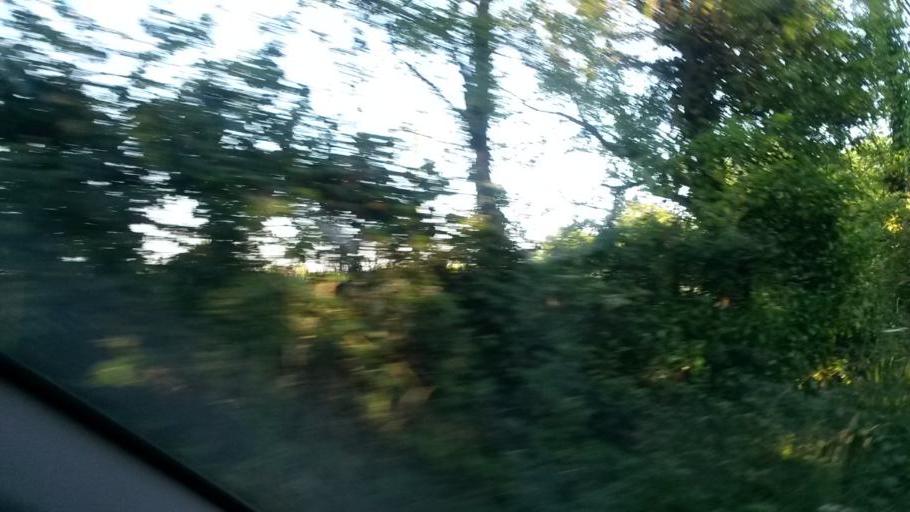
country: IE
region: Leinster
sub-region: An Mhi
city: Ashbourne
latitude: 53.5508
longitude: -6.3609
